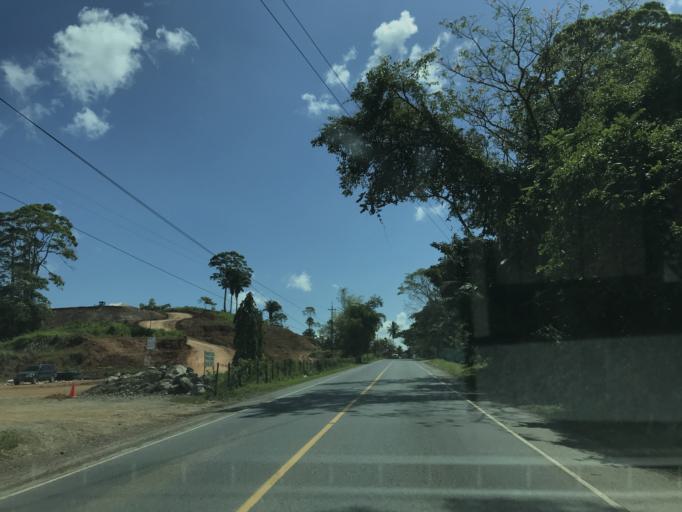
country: GT
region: Izabal
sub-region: Municipio de Puerto Barrios
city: Puerto Barrios
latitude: 15.6630
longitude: -88.5531
